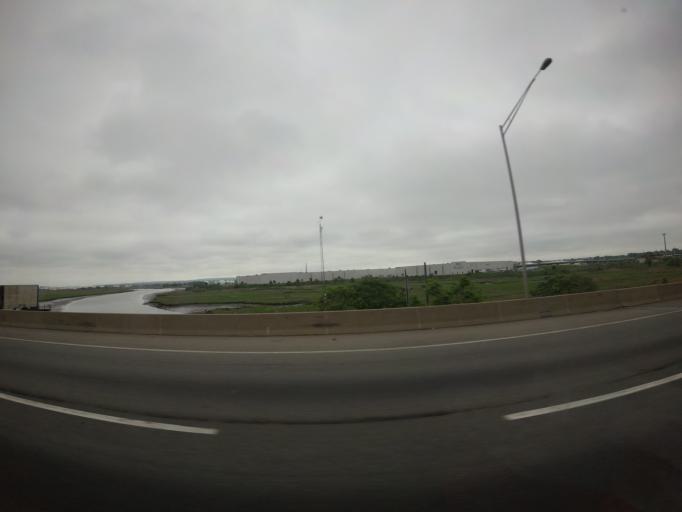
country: US
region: New Jersey
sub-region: Middlesex County
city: Carteret
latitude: 40.5985
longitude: -74.2316
